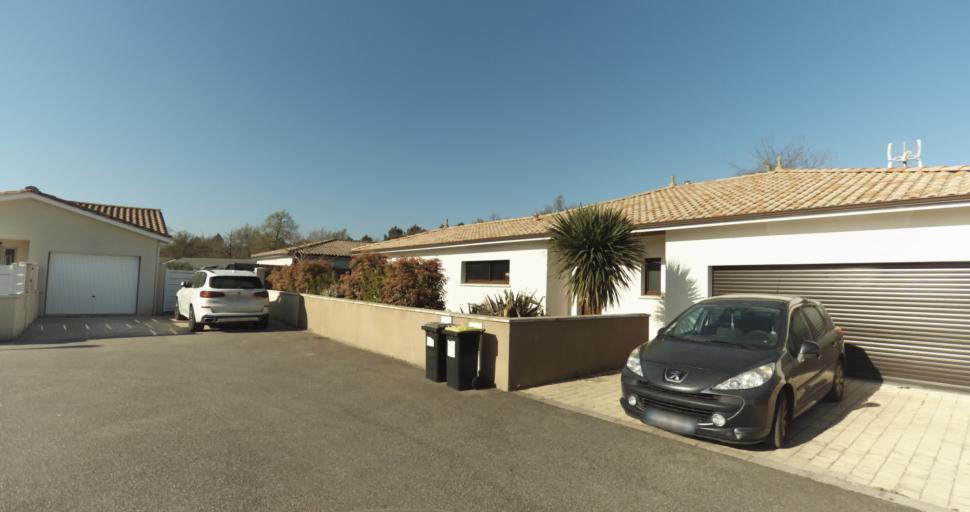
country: FR
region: Aquitaine
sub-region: Departement de la Gironde
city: Martignas-sur-Jalle
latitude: 44.8033
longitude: -0.7962
